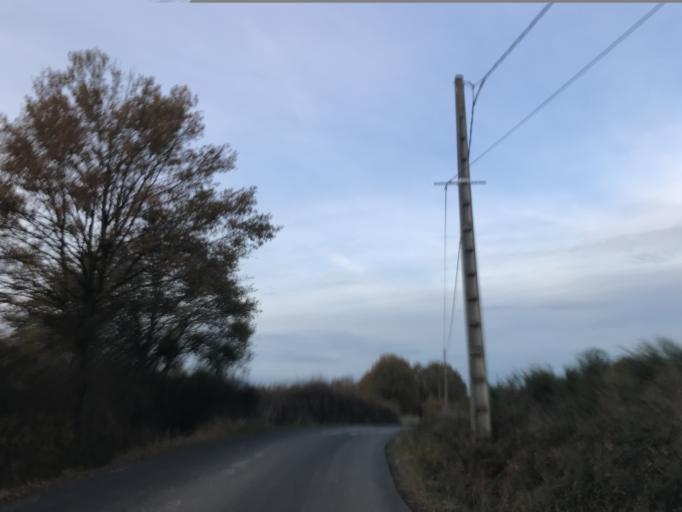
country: FR
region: Auvergne
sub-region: Departement du Puy-de-Dome
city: Courpiere
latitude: 45.7713
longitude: 3.5039
